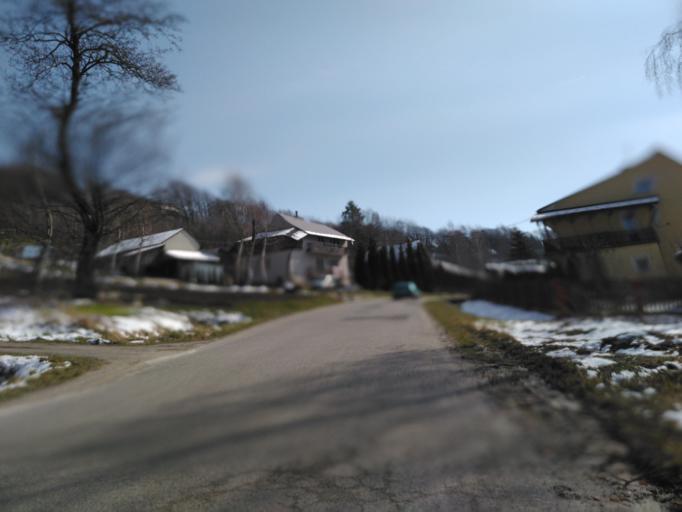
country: PL
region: Subcarpathian Voivodeship
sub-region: Powiat ropczycko-sedziszowski
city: Wielopole Skrzynskie
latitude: 49.9891
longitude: 21.5830
